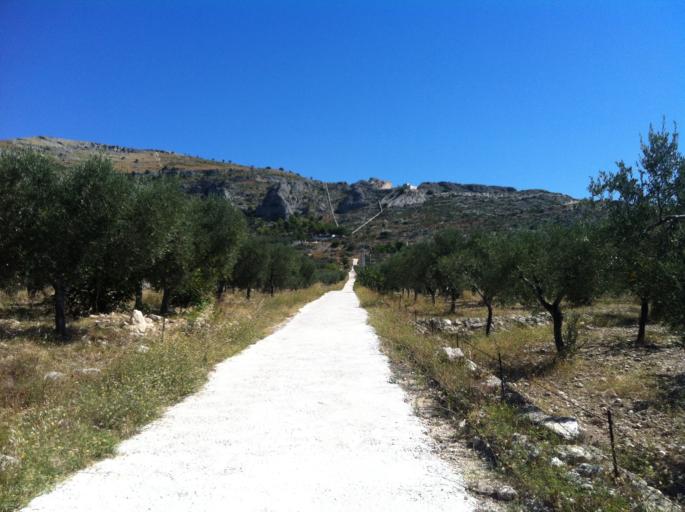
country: IT
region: Apulia
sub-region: Provincia di Foggia
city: Manfredonia
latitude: 41.6595
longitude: 15.9137
